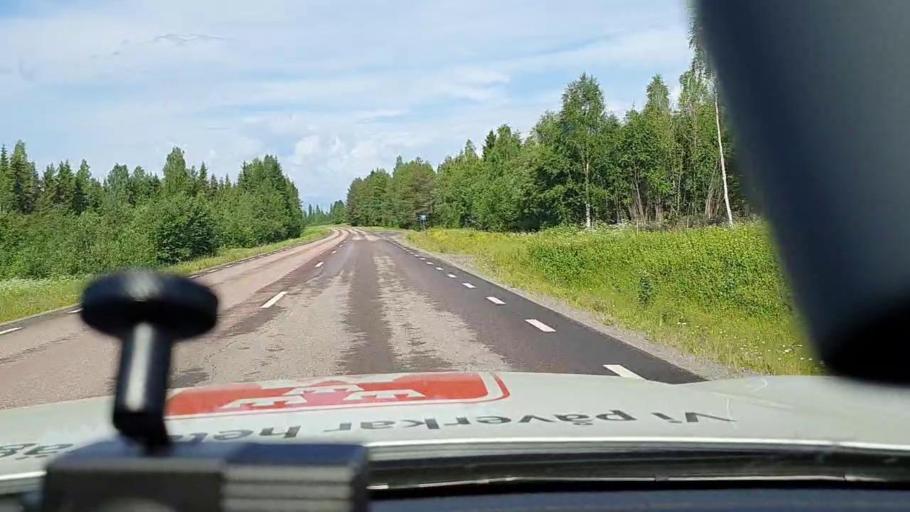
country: SE
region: Norrbotten
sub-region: Alvsbyns Kommun
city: AElvsbyn
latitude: 66.0213
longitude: 21.1342
